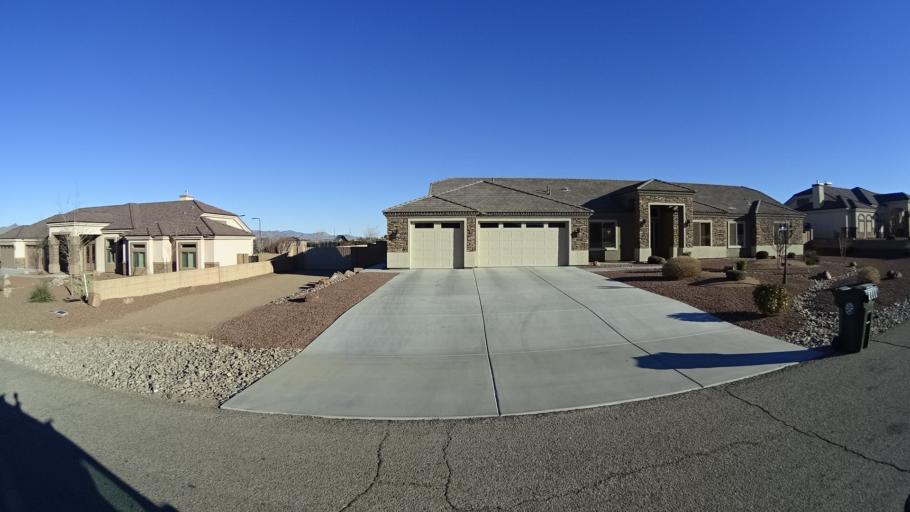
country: US
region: Arizona
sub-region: Mohave County
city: Kingman
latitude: 35.1949
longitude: -113.9997
